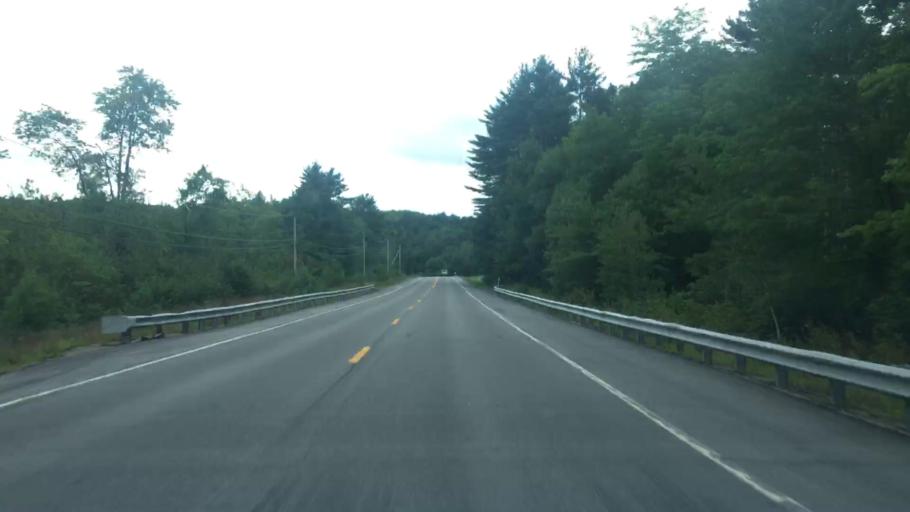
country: US
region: Maine
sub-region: York County
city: Cornish
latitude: 43.7588
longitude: -70.8159
